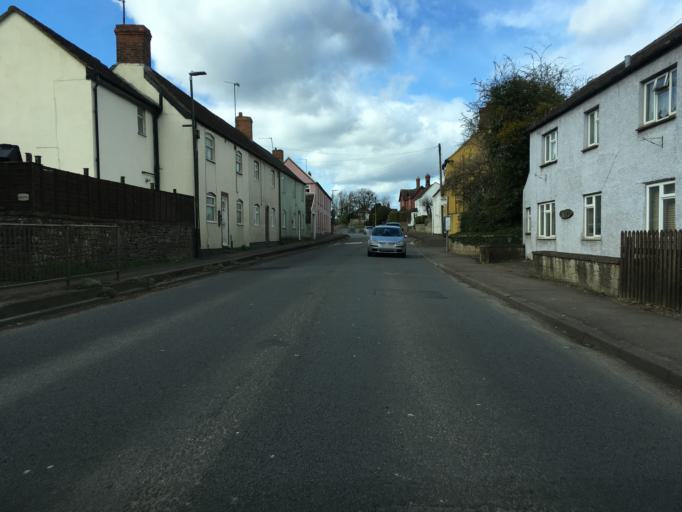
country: GB
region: England
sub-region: Gloucestershire
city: Cinderford
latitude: 51.8249
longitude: -2.4128
